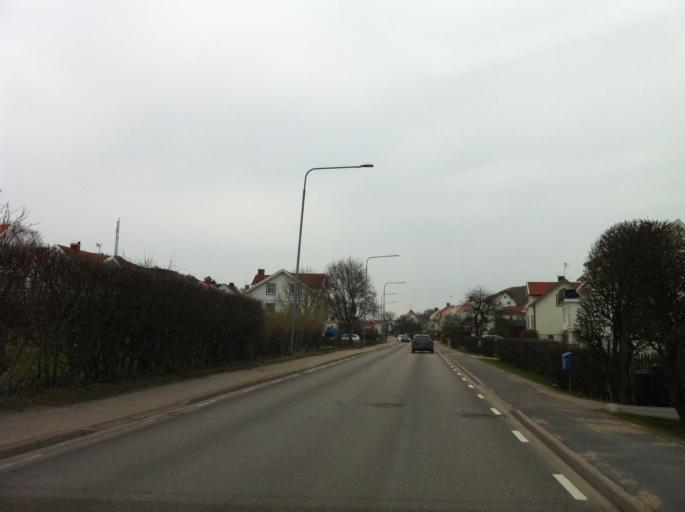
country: SE
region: Vaestra Goetaland
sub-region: Orust
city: Henan
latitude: 58.1737
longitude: 11.6985
